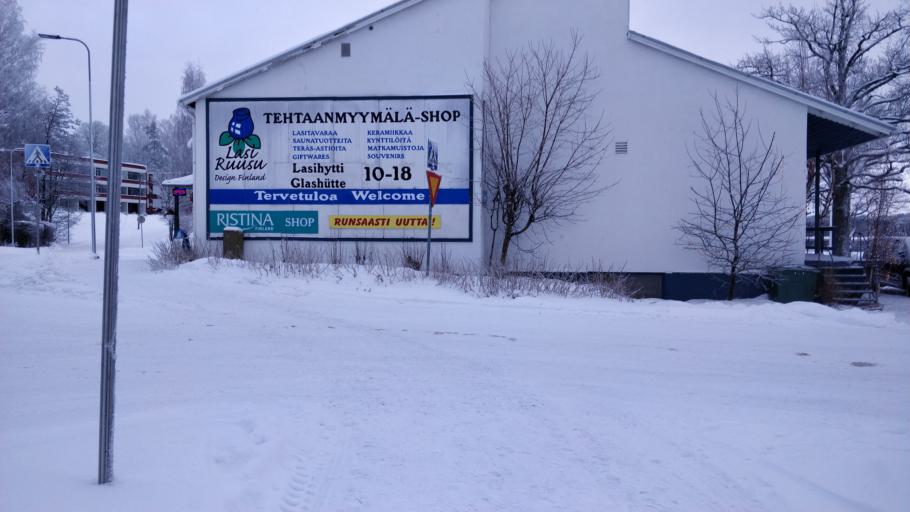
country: FI
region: Southern Savonia
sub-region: Mikkeli
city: Puumala
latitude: 61.5204
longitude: 28.1787
